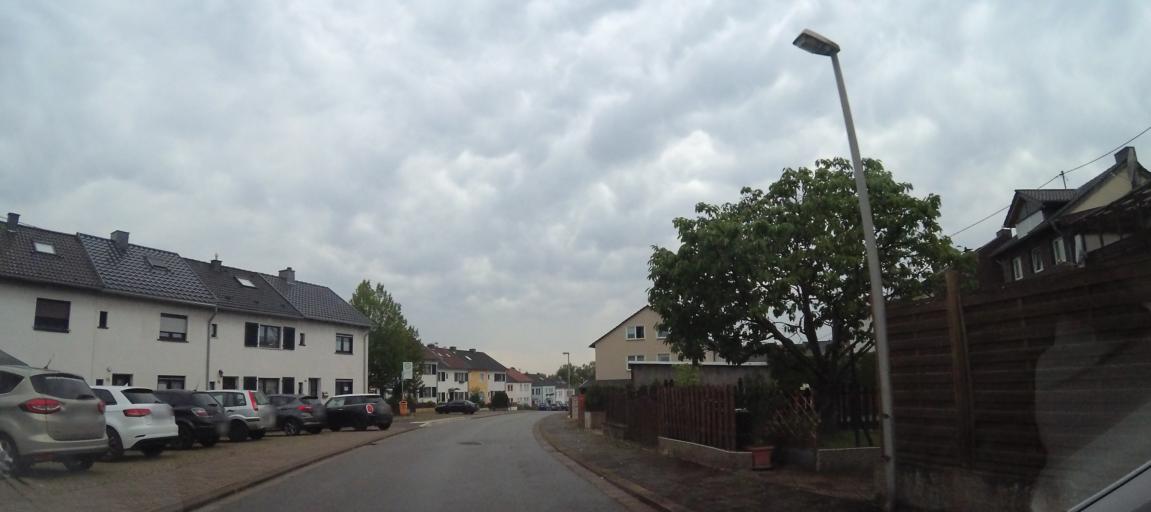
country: DE
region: Saarland
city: Saarwellingen
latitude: 49.3327
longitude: 6.7891
